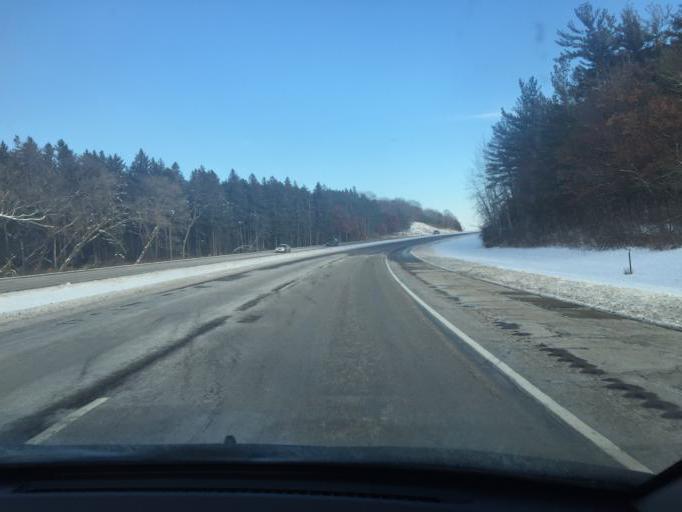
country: US
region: Minnesota
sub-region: Olmsted County
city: Rochester
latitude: 44.0118
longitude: -92.4298
